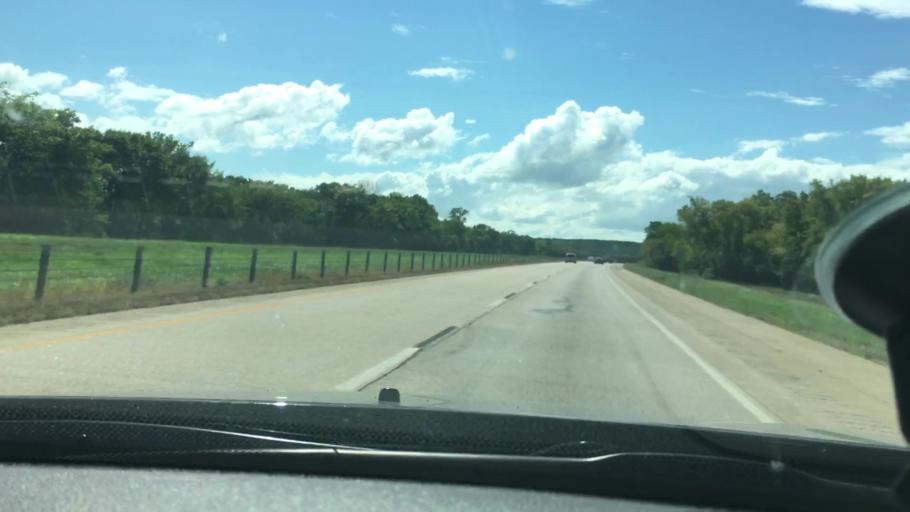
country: US
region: Oklahoma
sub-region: Sequoyah County
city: Vian
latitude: 35.4916
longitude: -95.0179
